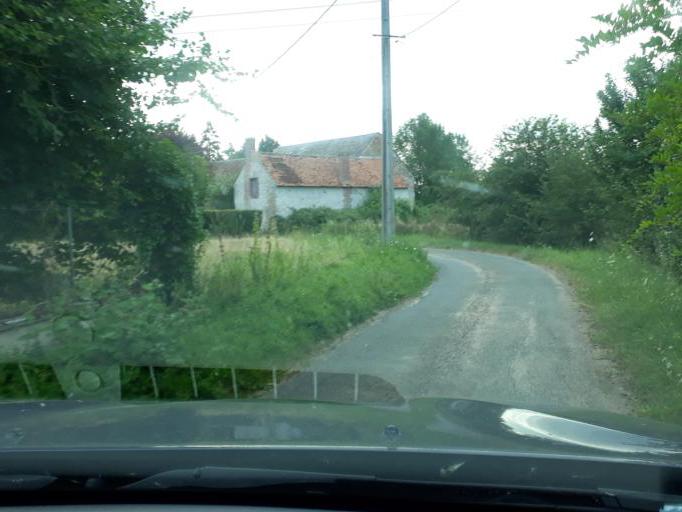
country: FR
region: Centre
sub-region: Departement du Loiret
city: Tavers
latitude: 47.7461
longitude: 1.6313
